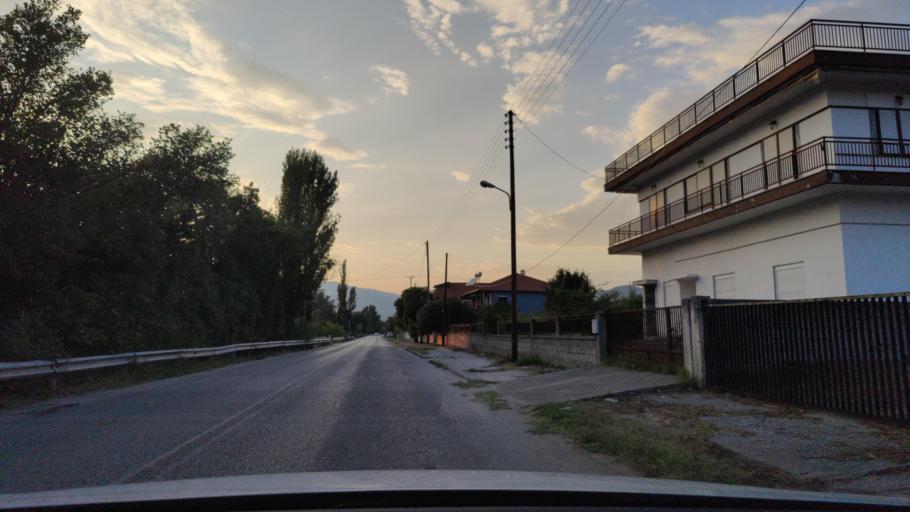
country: GR
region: Central Macedonia
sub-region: Nomos Serron
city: Sidirokastro
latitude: 41.2428
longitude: 23.3839
